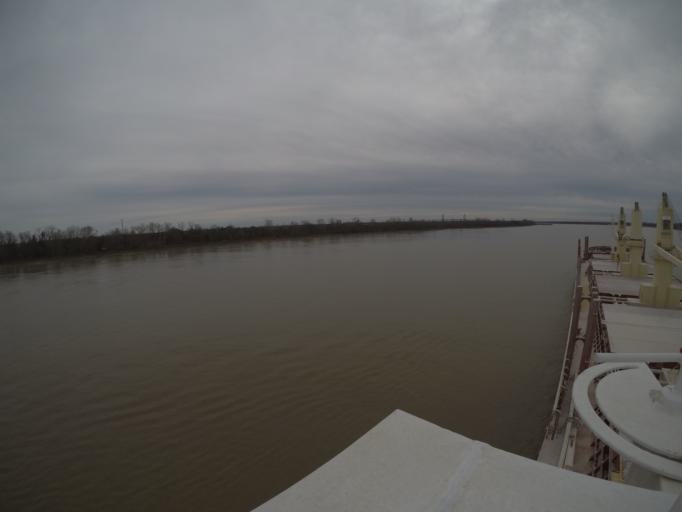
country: US
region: Louisiana
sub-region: Saint Charles Parish
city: New Sarpy
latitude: 29.9754
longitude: -90.3959
